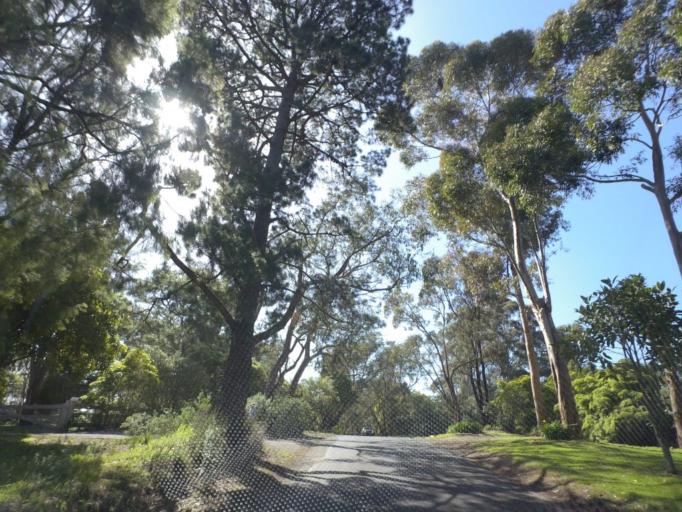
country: AU
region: Victoria
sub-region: Manningham
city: Park Orchards
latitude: -37.7869
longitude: 145.2268
